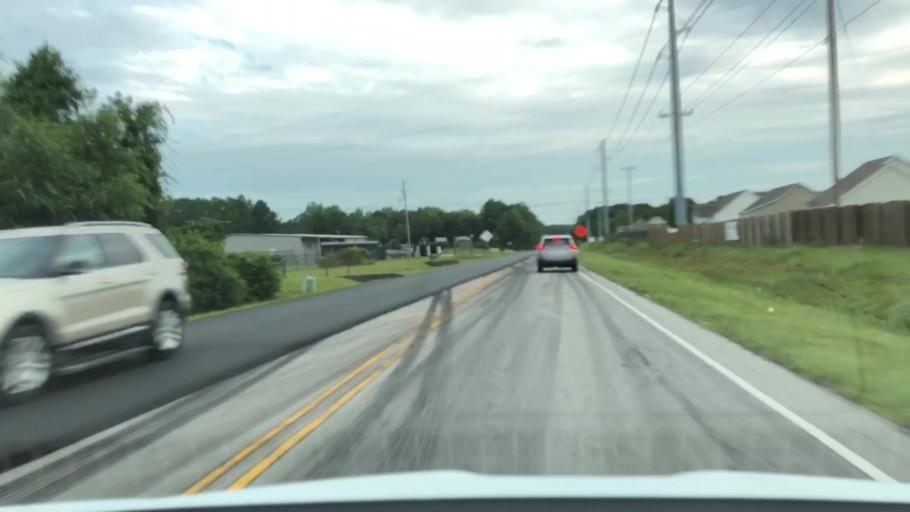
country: US
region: North Carolina
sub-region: Carteret County
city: Cape Carteret
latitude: 34.7593
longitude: -77.0945
